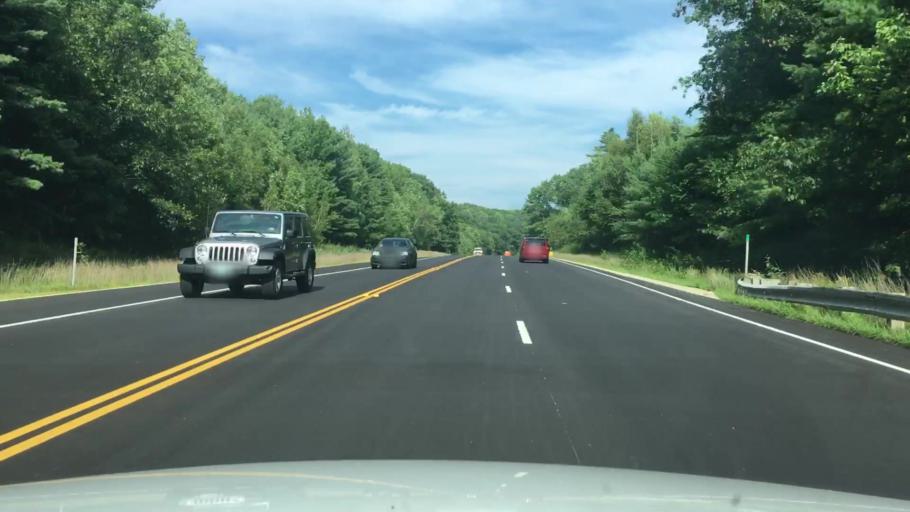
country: US
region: New Hampshire
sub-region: Belknap County
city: Gilford
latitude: 43.5397
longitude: -71.4291
